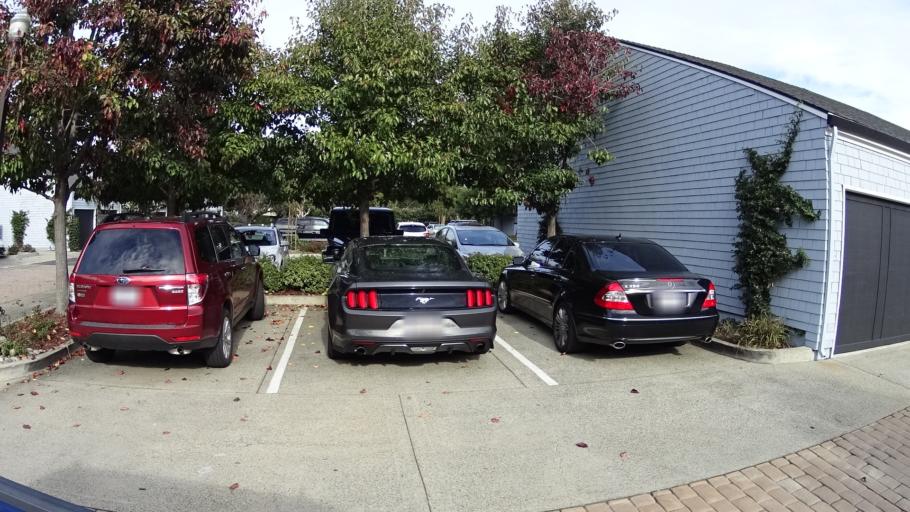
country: US
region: California
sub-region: San Mateo County
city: Redwood Shores
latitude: 37.5359
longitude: -122.2472
